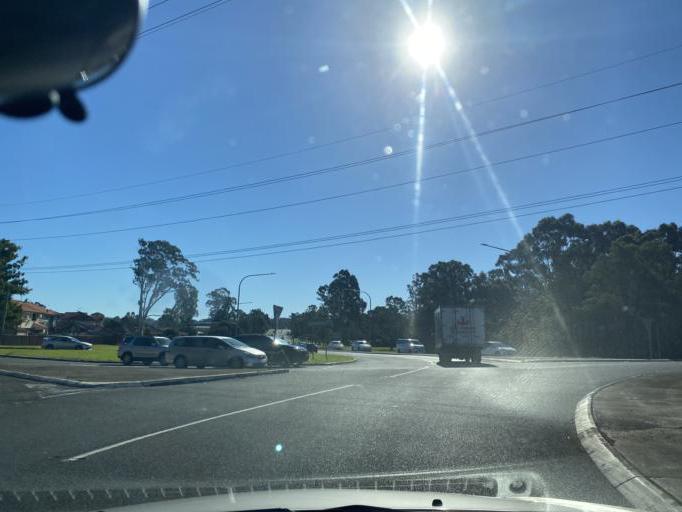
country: AU
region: New South Wales
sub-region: Campbelltown Municipality
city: Ingleburn
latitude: -33.9950
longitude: 150.8753
